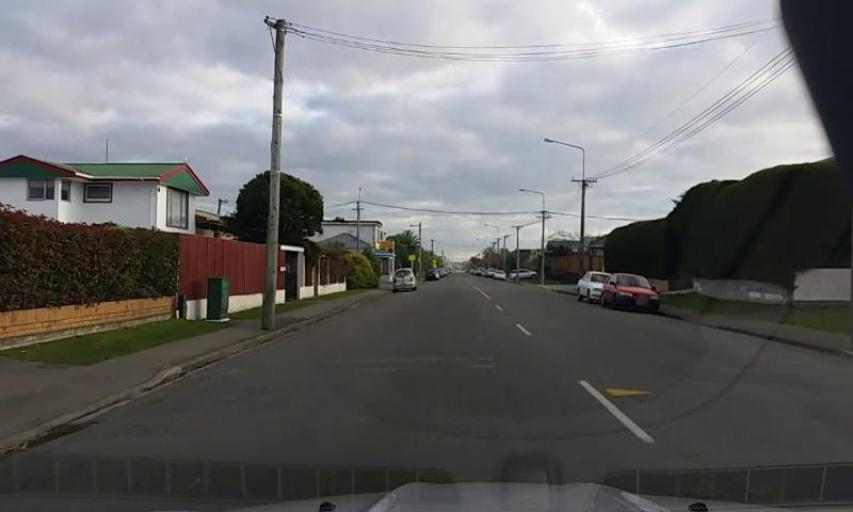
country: NZ
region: Canterbury
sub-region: Christchurch City
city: Christchurch
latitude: -43.5284
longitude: 172.7349
